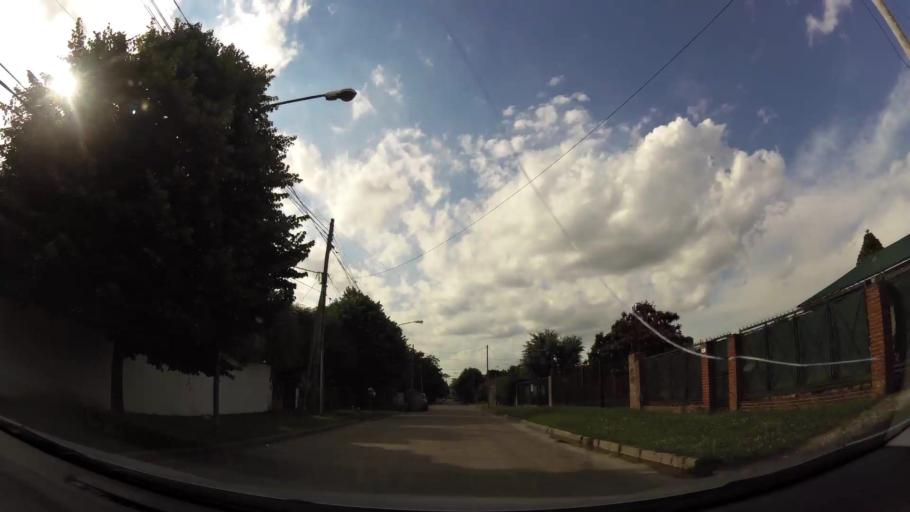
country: AR
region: Buenos Aires
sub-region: Partido de Tigre
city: Tigre
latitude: -34.4756
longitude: -58.6531
